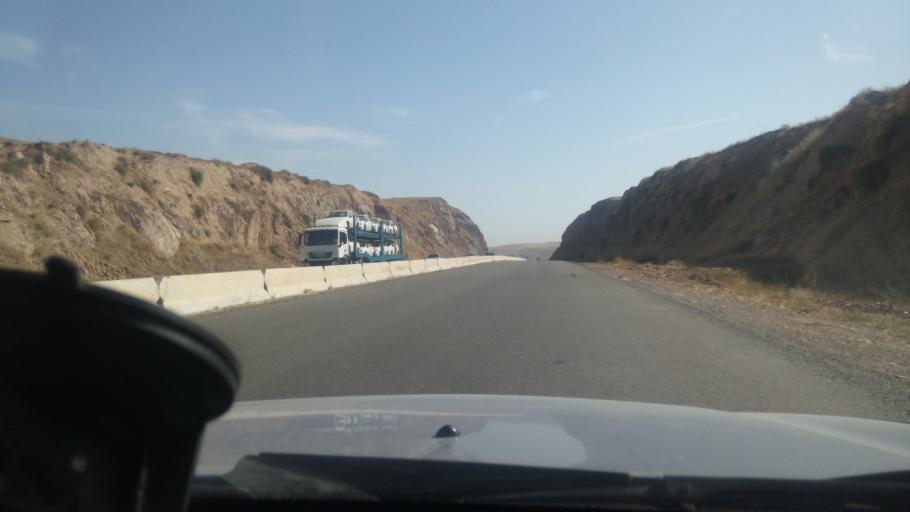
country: UZ
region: Jizzax
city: Jizzax
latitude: 40.0477
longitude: 67.6764
